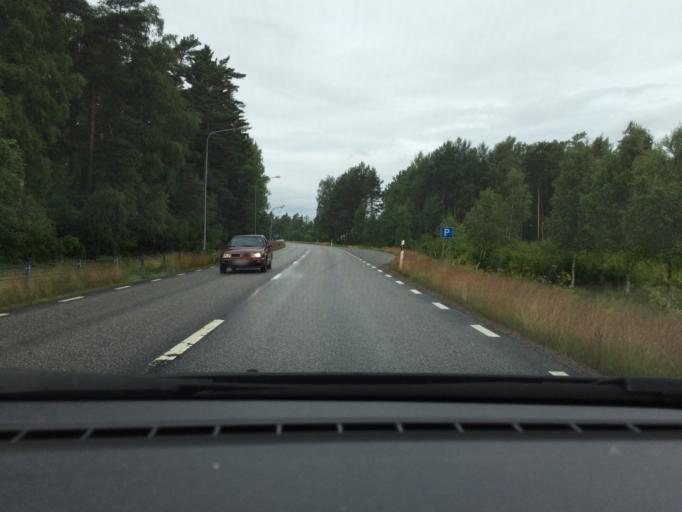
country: SE
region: Joenkoeping
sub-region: Varnamo Kommun
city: Forsheda
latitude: 57.1651
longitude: 13.8399
